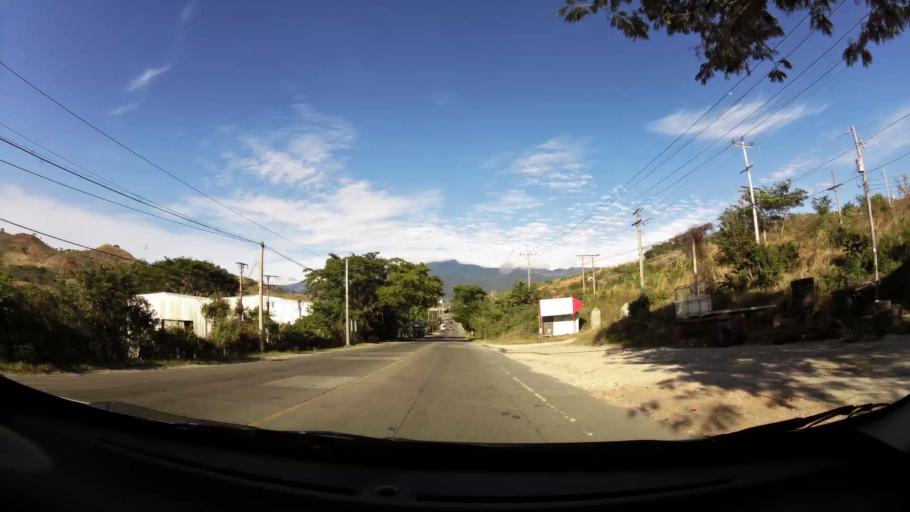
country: SV
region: Santa Ana
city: Metapan
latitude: 14.3115
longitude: -89.4511
